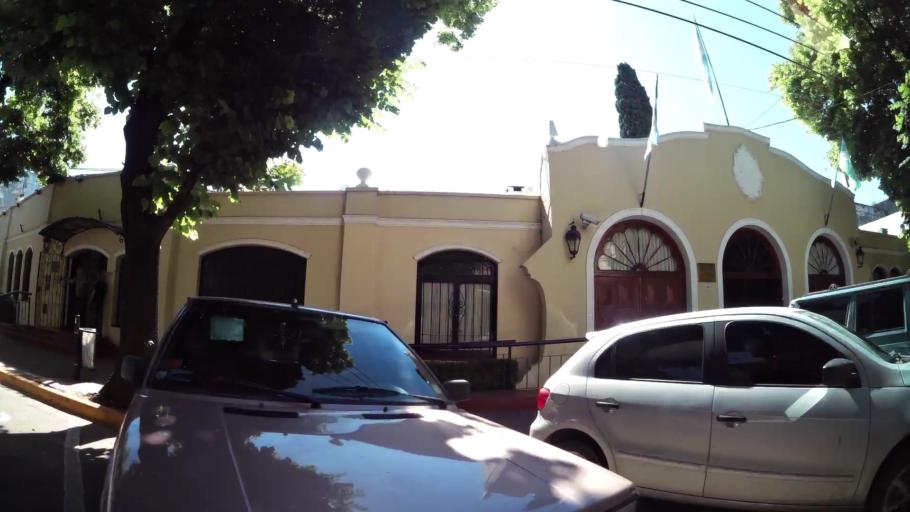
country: AR
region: Buenos Aires
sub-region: Partido de San Isidro
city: San Isidro
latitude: -34.4679
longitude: -58.5104
